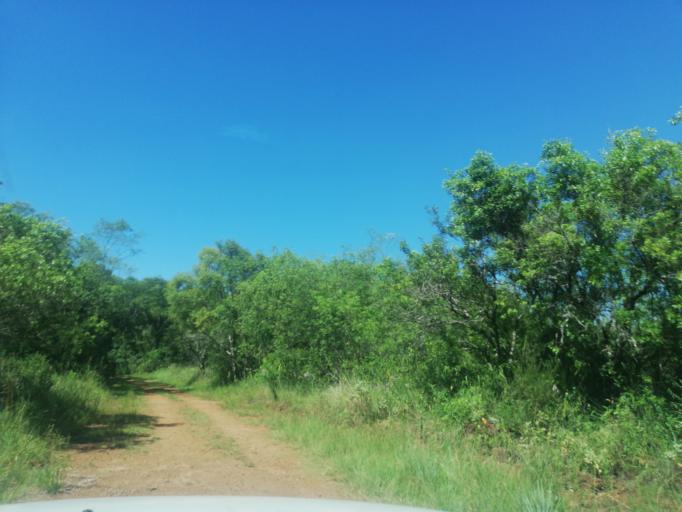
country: AR
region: Misiones
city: Cerro Azul
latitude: -27.7426
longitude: -55.5728
